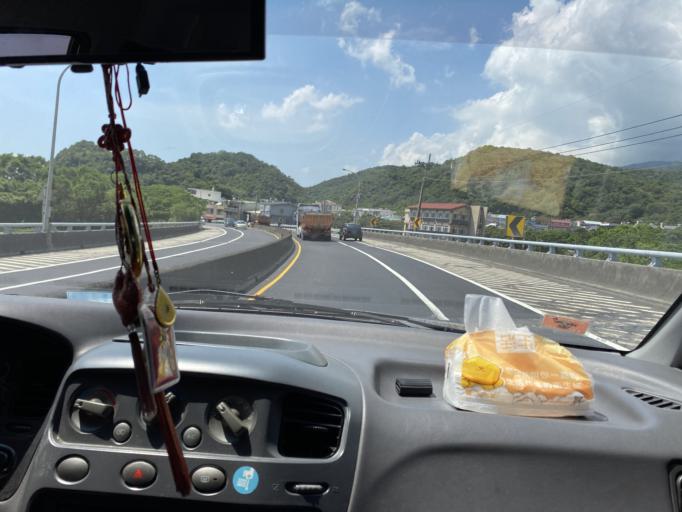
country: TW
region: Taiwan
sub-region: Yilan
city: Yilan
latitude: 24.9032
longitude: 121.8647
